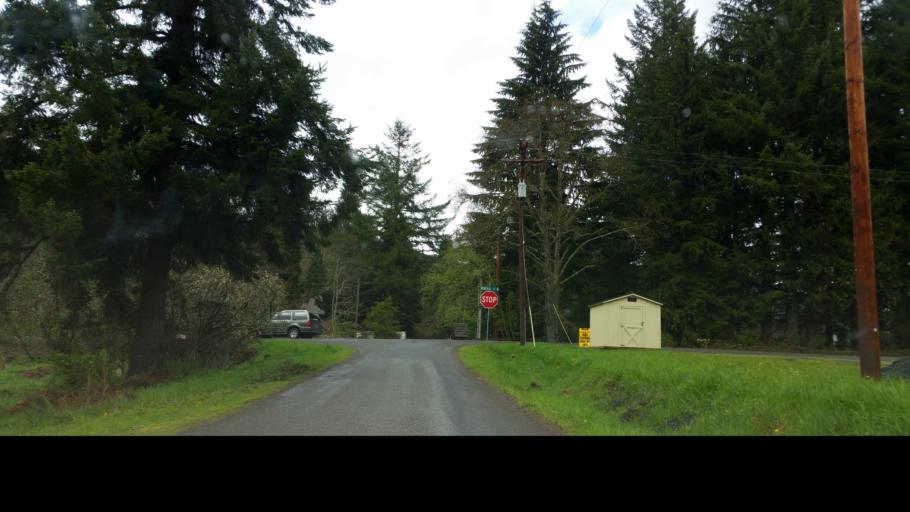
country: US
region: Washington
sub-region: Pierce County
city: Eatonville
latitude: 46.7182
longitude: -122.1834
